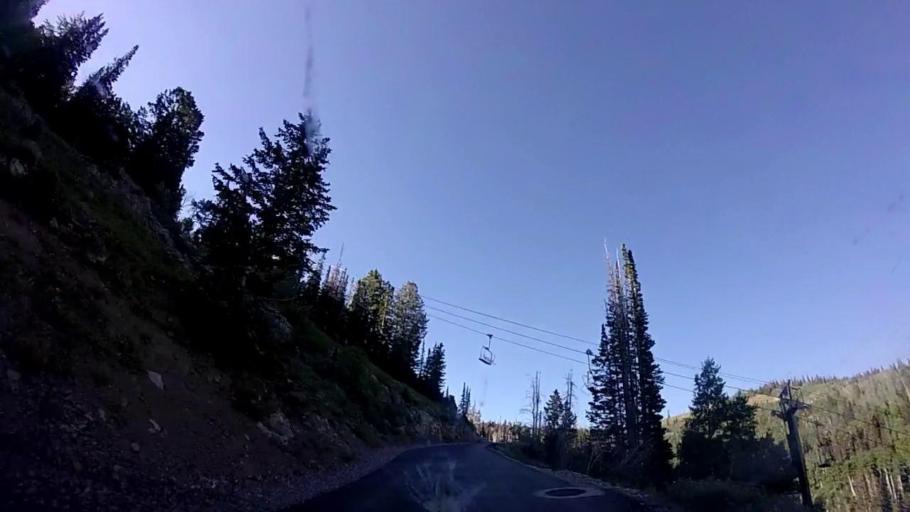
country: US
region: Utah
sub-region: Summit County
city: Park City
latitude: 40.6133
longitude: -111.5067
